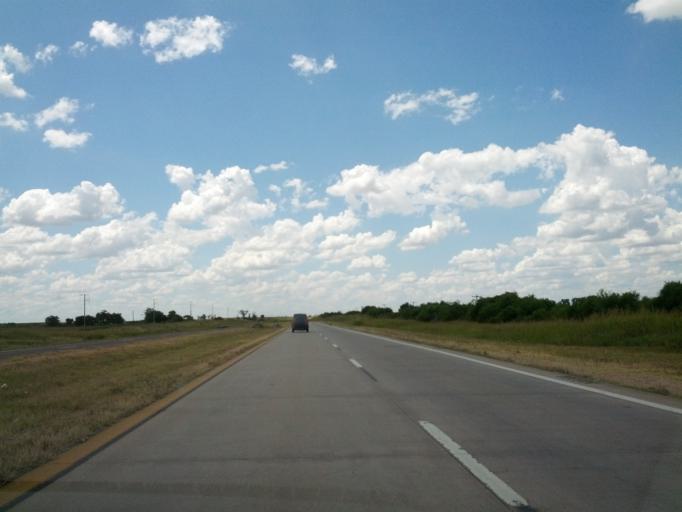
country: AR
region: Entre Rios
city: Gualeguaychu
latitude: -32.9320
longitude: -58.5720
